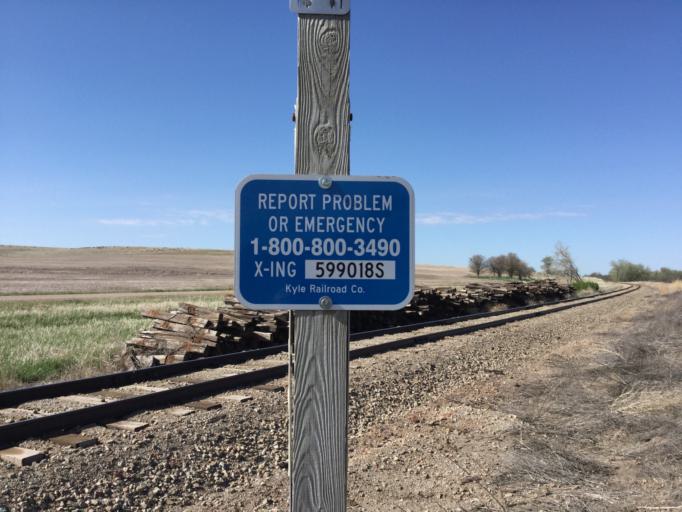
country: US
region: Kansas
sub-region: Decatur County
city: Oberlin
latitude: 39.7120
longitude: -100.2472
